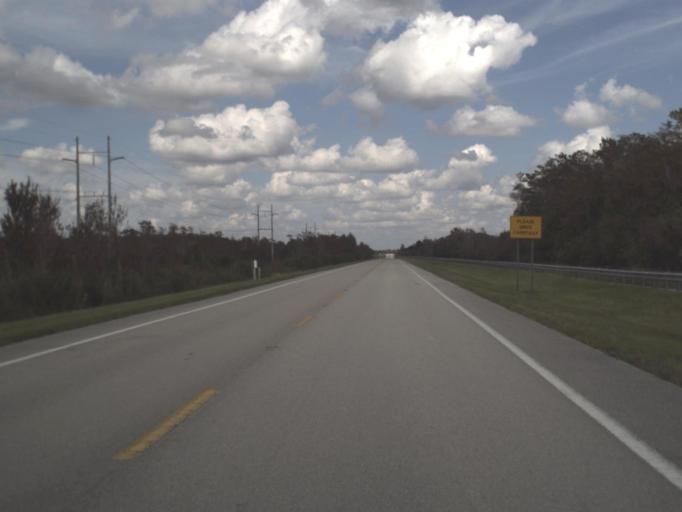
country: US
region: Florida
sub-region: Collier County
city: Lely Resort
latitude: 25.9688
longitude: -81.3525
